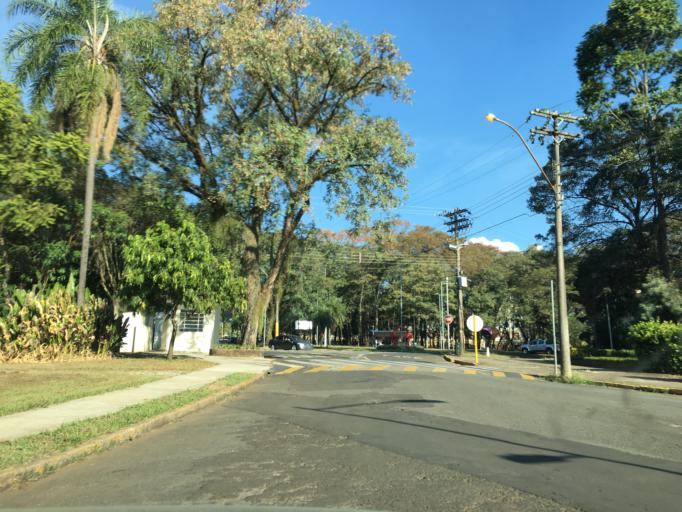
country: BR
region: Sao Paulo
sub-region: Piracicaba
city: Piracicaba
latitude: -22.7106
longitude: -47.6356
